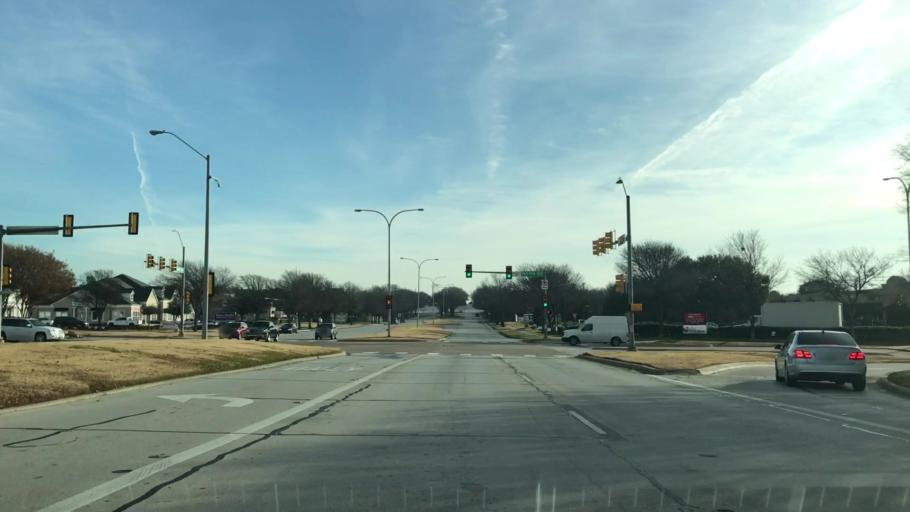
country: US
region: Texas
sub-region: Tarrant County
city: Watauga
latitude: 32.8742
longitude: -97.2696
